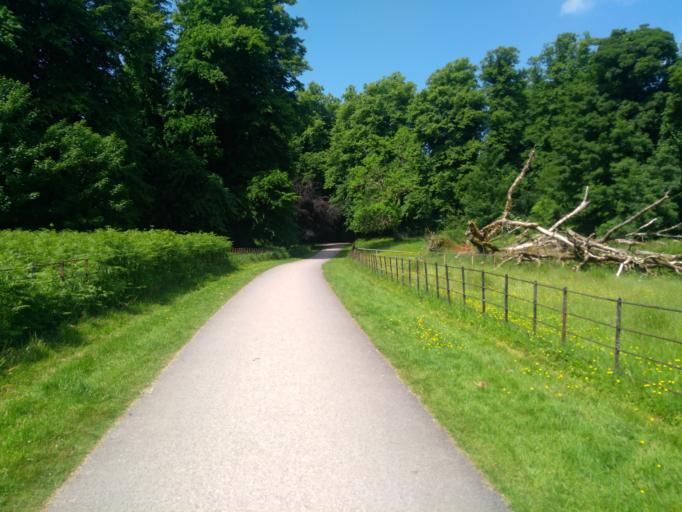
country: IE
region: Munster
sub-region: Ciarrai
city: Cill Airne
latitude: 52.0251
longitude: -9.4940
